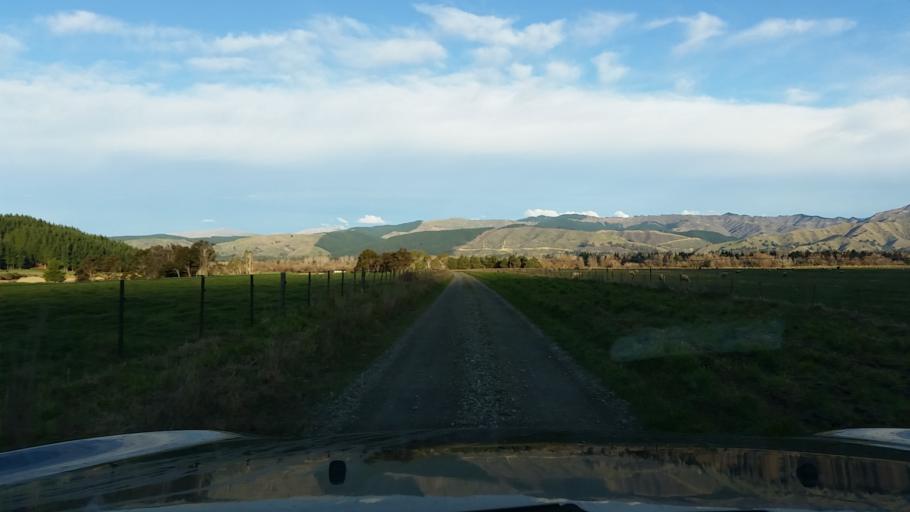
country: NZ
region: Nelson
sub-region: Nelson City
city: Nelson
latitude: -41.5364
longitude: 173.4906
